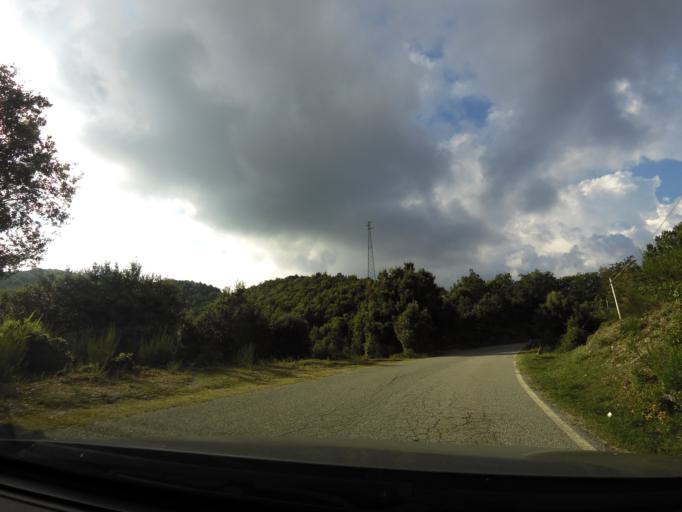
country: IT
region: Calabria
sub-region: Provincia di Vibo-Valentia
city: Nardodipace
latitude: 38.4793
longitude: 16.3824
